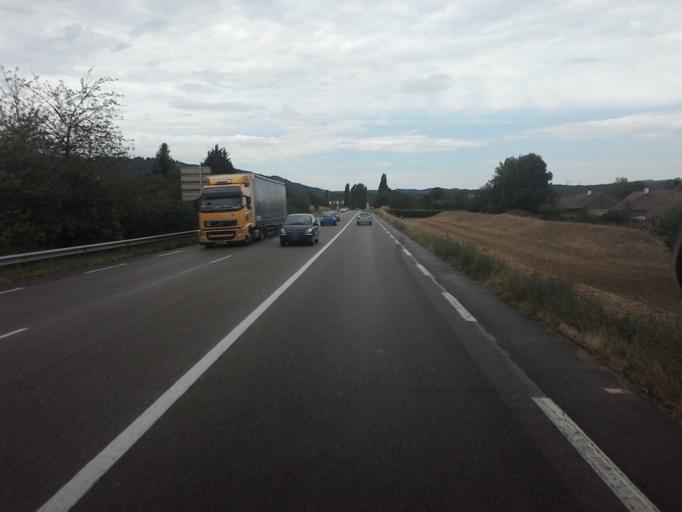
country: FR
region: Franche-Comte
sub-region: Departement du Jura
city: Poligny
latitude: 46.8421
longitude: 5.7003
